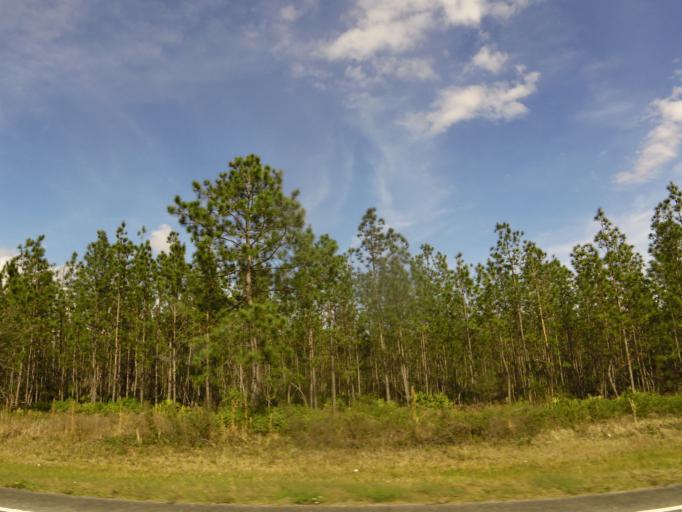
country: US
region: Florida
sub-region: Volusia County
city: Pierson
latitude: 29.2590
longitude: -81.3311
